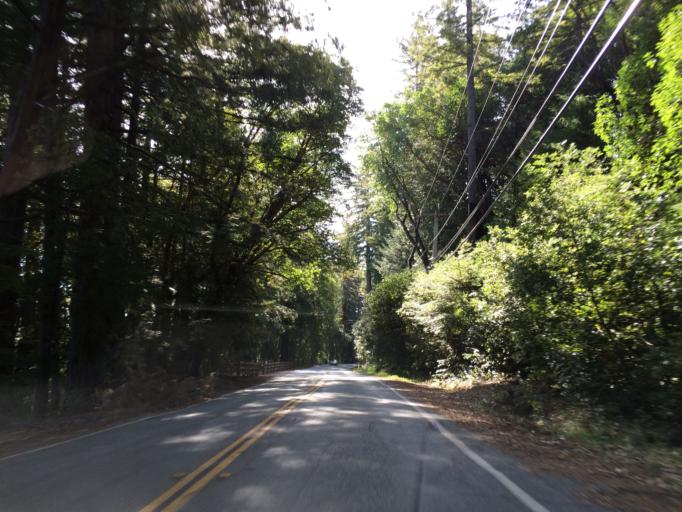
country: US
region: California
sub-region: Santa Cruz County
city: Brookdale
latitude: 37.0891
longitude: -122.1377
